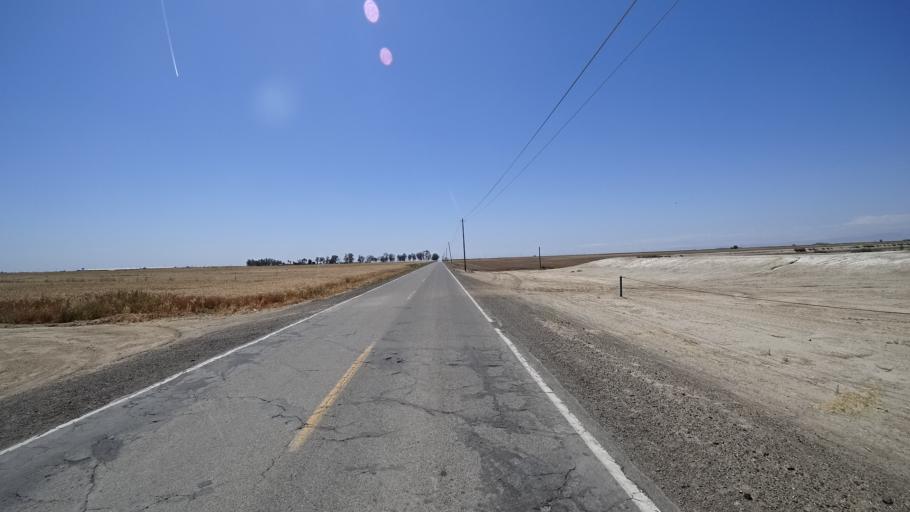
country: US
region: California
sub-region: Kings County
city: Armona
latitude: 36.2185
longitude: -119.7087
